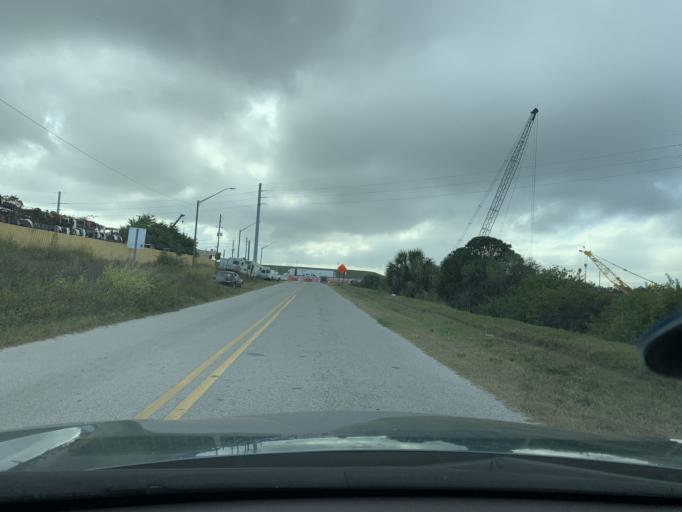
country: US
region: Florida
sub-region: Pinellas County
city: Pinellas Park
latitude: 27.8809
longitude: -82.6880
